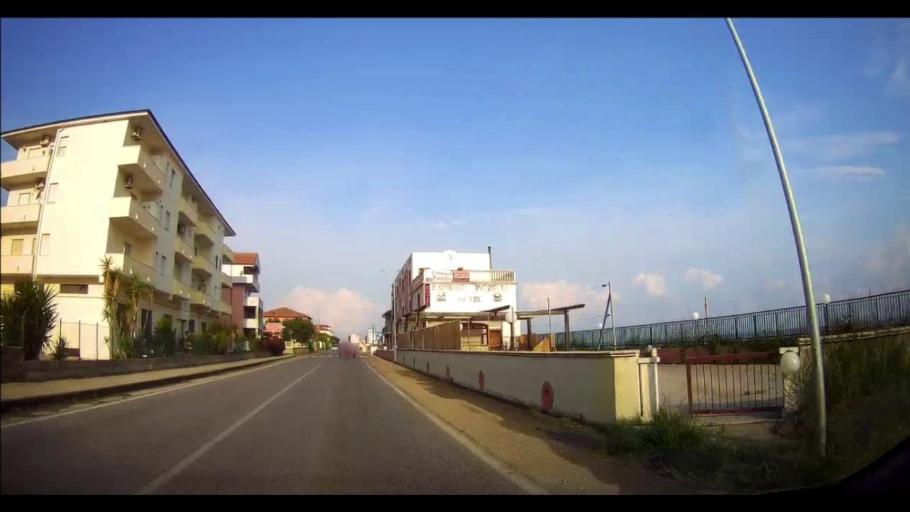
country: IT
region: Calabria
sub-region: Provincia di Cosenza
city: Cariati
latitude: 39.5091
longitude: 16.9314
